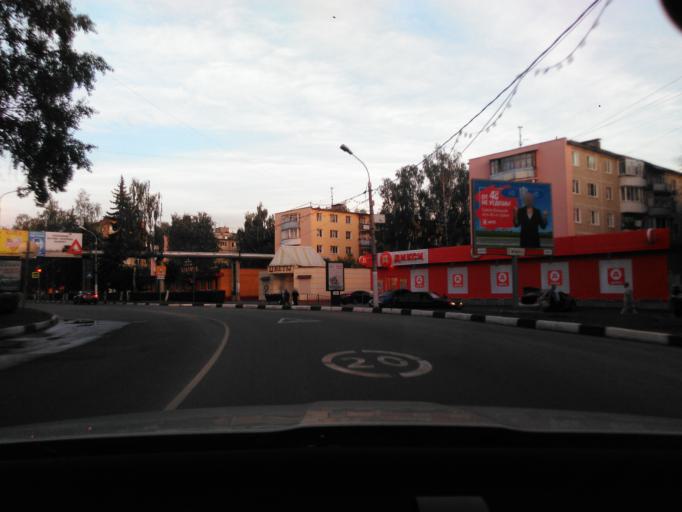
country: RU
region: Moskovskaya
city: Klin
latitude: 56.3201
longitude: 36.7233
